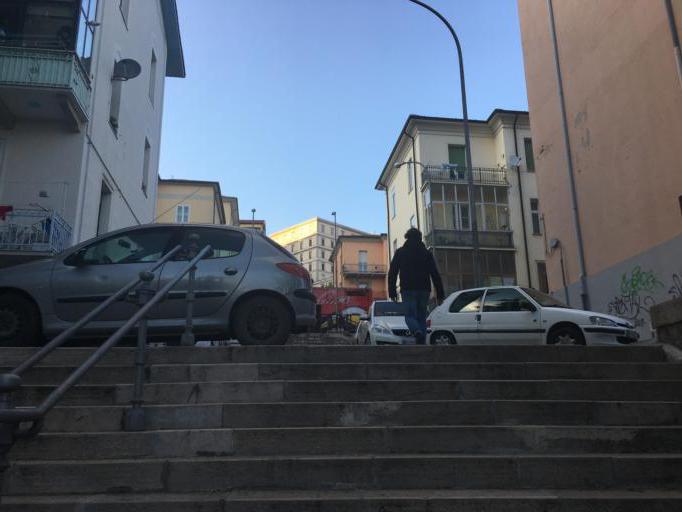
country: IT
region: Basilicate
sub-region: Provincia di Potenza
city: Potenza
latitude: 40.6362
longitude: 15.8056
